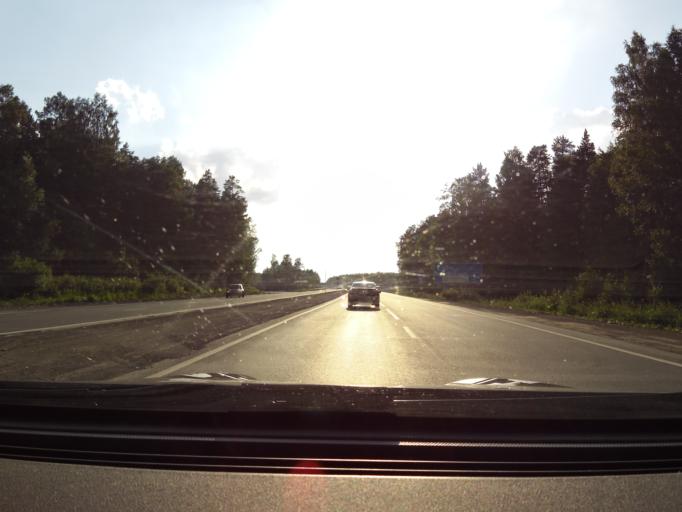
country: RU
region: Sverdlovsk
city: Talitsa
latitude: 56.8487
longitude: 60.0683
